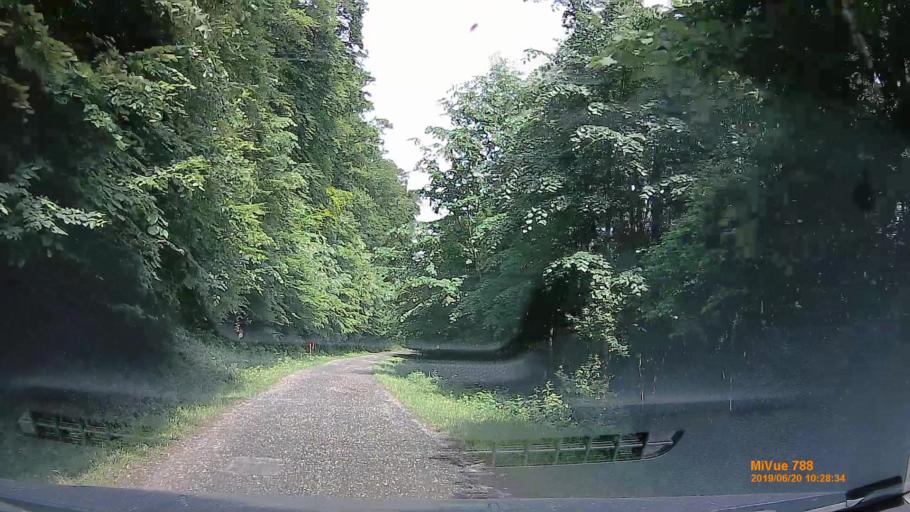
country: HU
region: Baranya
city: Mecseknadasd
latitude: 46.2070
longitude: 18.4938
